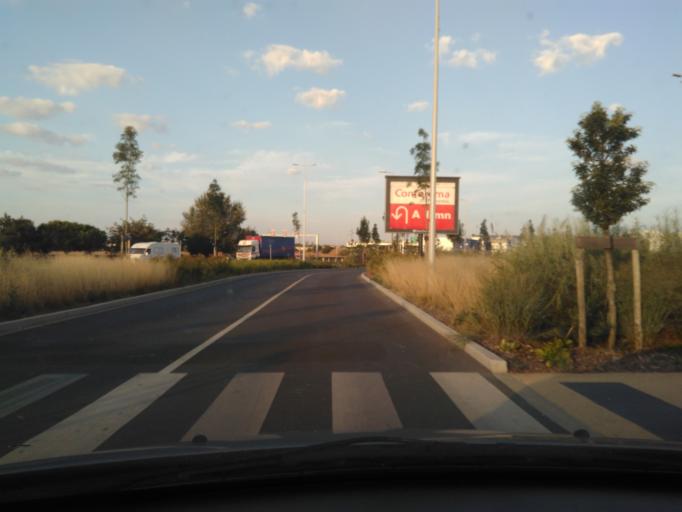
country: FR
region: Poitou-Charentes
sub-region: Departement de la Charente-Maritime
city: Puilboreau
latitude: 46.1742
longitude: -1.1158
